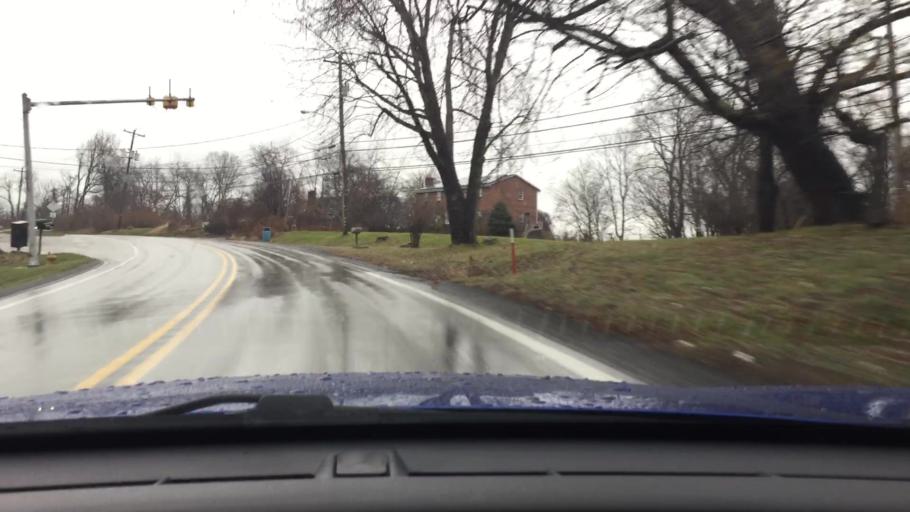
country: US
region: Pennsylvania
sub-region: Allegheny County
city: Wilson
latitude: 40.3156
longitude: -79.9173
